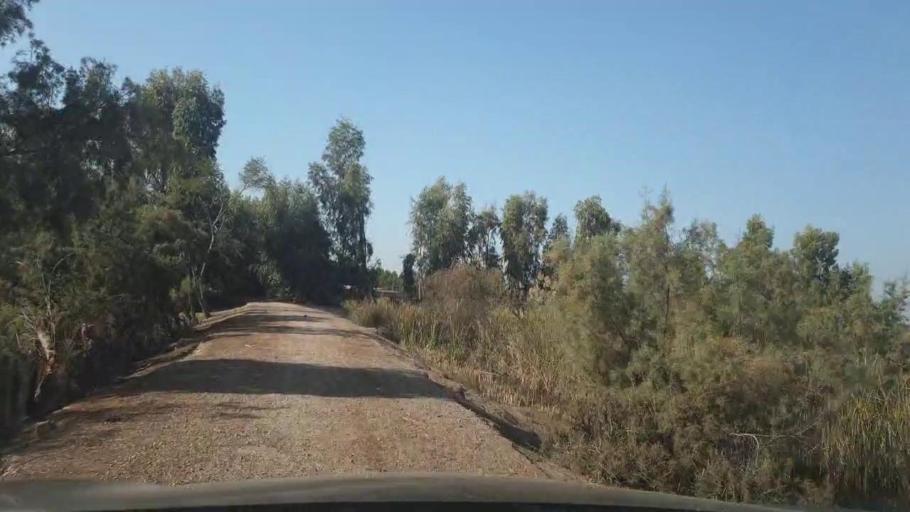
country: PK
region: Sindh
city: Khairpur
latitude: 28.1387
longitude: 69.5984
